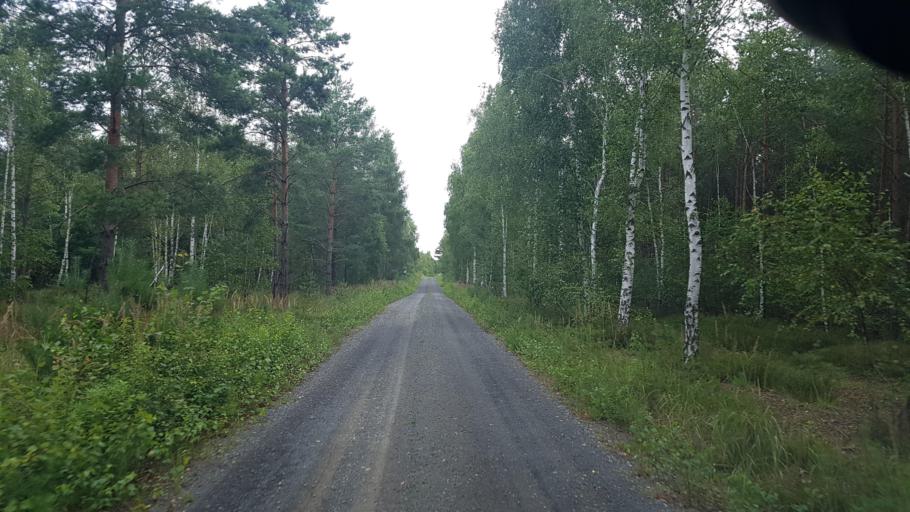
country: DE
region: Brandenburg
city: Grossraschen
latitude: 51.6208
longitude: 13.9686
